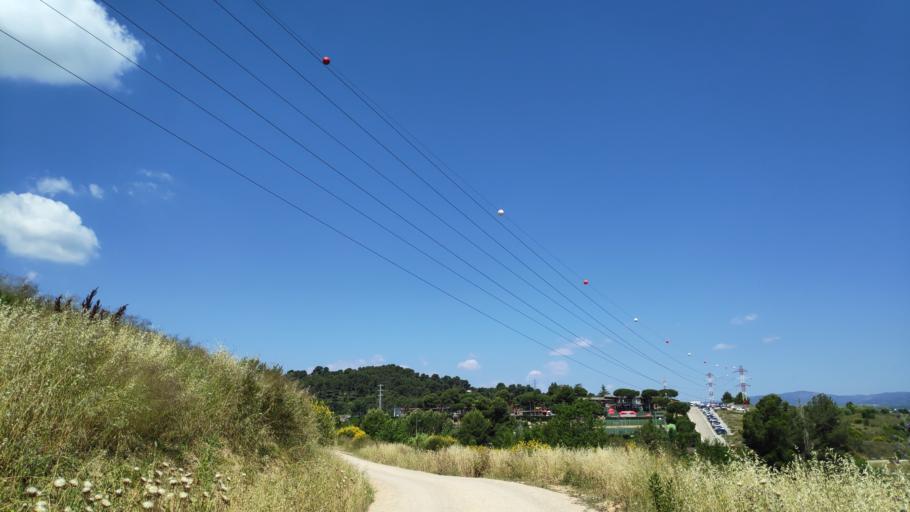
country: ES
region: Catalonia
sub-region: Provincia de Barcelona
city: Barbera del Valles
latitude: 41.5122
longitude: 2.0996
